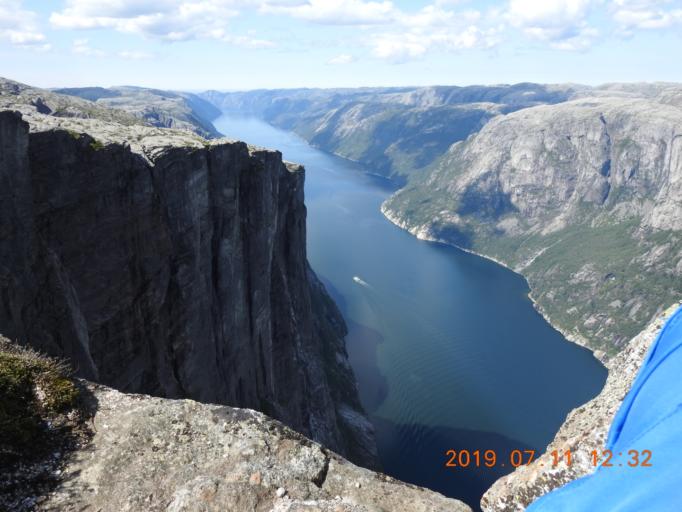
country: NO
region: Vest-Agder
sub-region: Sirdal
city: Tonstad
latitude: 59.0357
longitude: 6.5916
